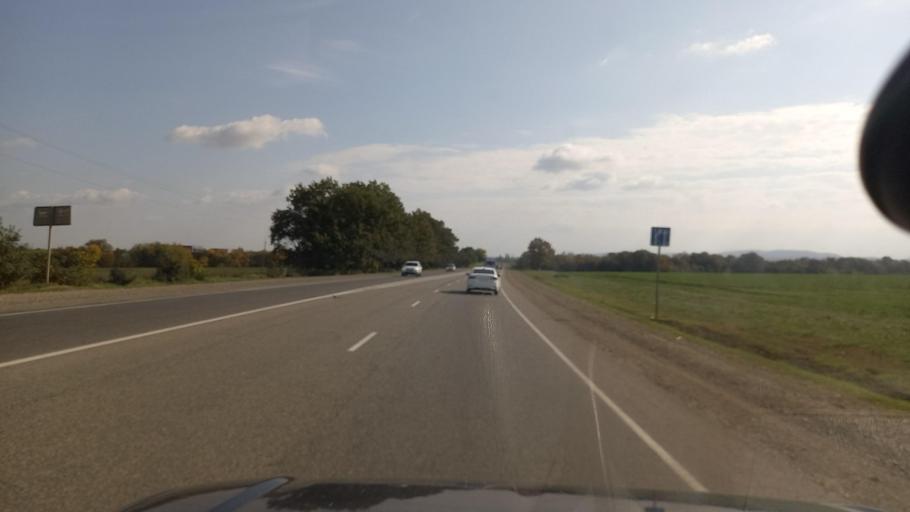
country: RU
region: Krasnodarskiy
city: Kholmskiy
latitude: 44.8549
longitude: 38.3509
